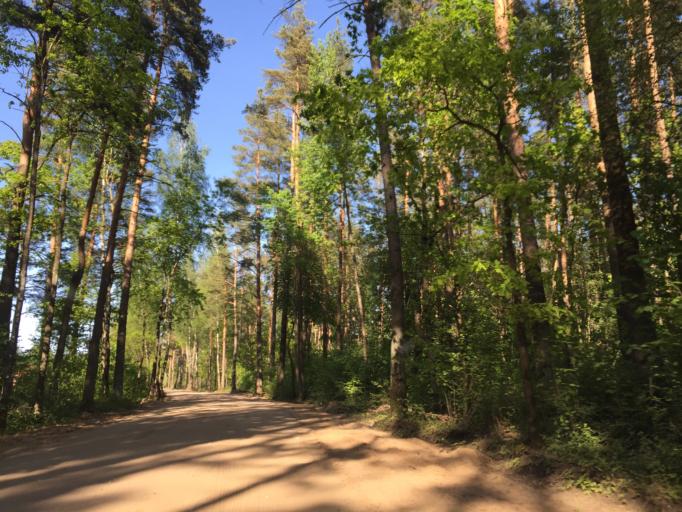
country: LV
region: Kekava
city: Kekava
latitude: 56.8180
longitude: 24.2314
